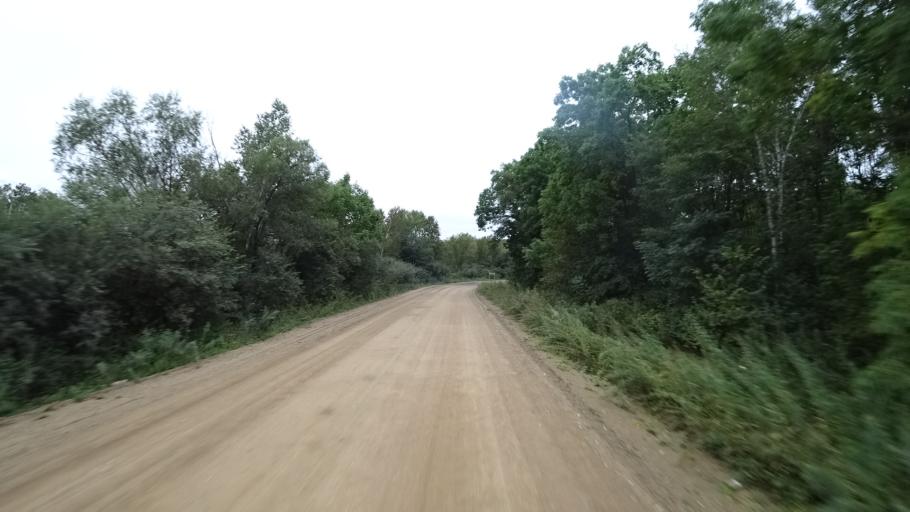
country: RU
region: Primorskiy
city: Rettikhovka
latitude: 44.1794
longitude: 132.8519
